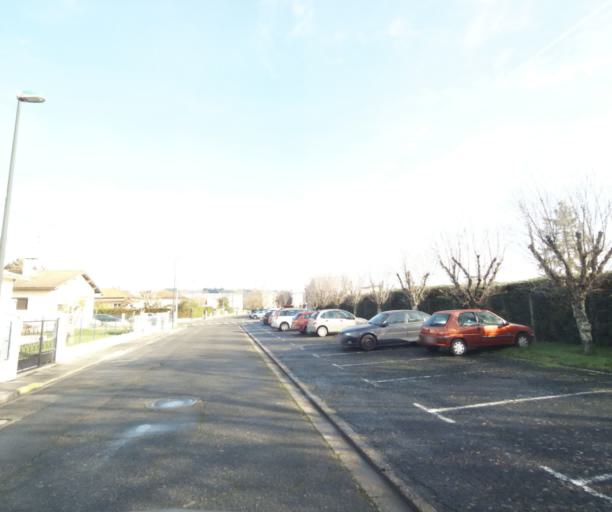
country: FR
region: Midi-Pyrenees
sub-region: Departement de la Haute-Garonne
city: Villemur-sur-Tarn
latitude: 43.8617
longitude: 1.4961
